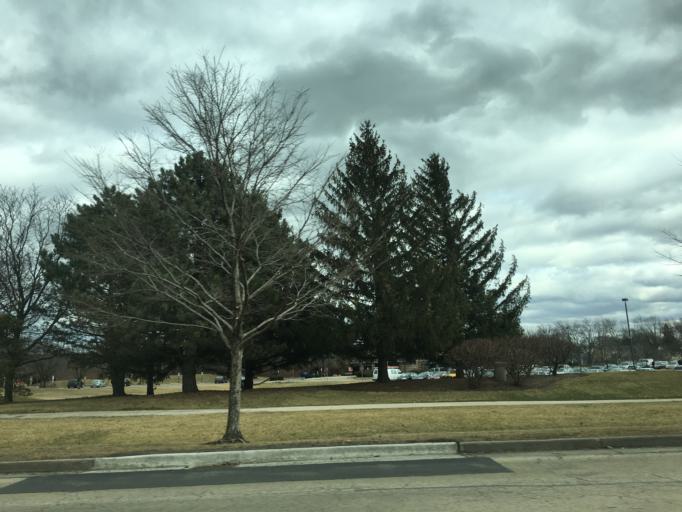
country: US
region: Illinois
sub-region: Cook County
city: Schaumburg
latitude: 42.0357
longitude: -88.1192
